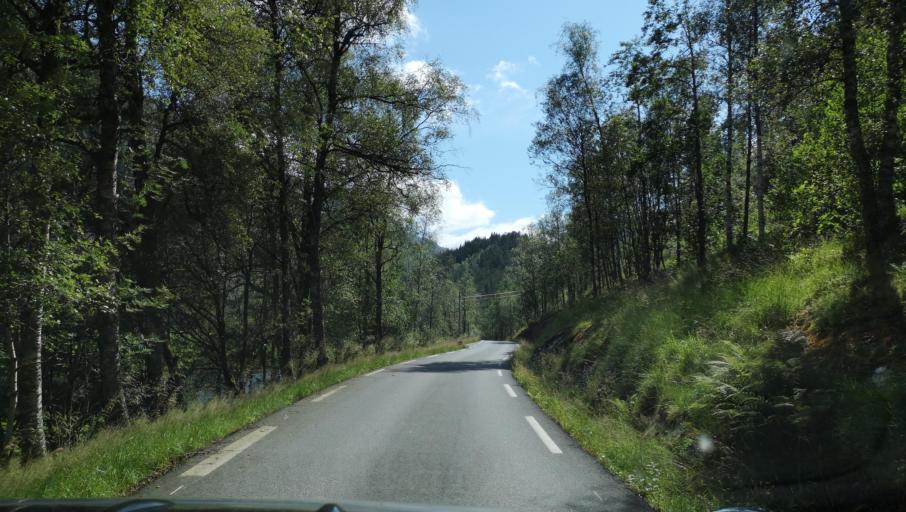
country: NO
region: Hordaland
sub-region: Modalen
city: Mo
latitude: 60.7837
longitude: 5.9484
